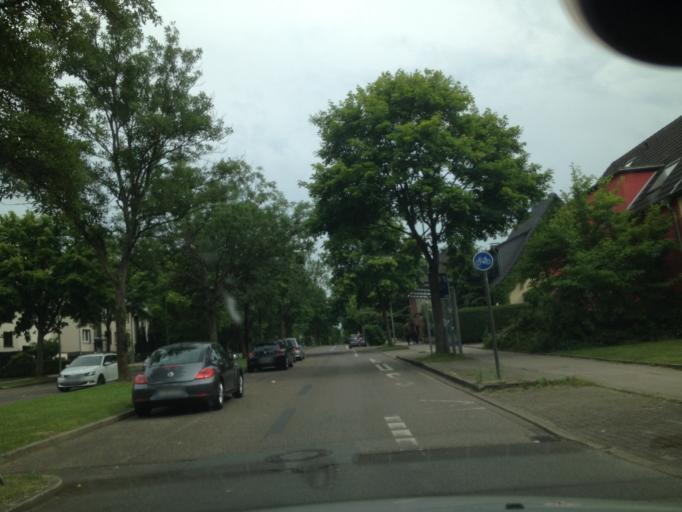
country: DE
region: North Rhine-Westphalia
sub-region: Regierungsbezirk Munster
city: Gelsenkirchen
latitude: 51.4369
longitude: 7.1073
